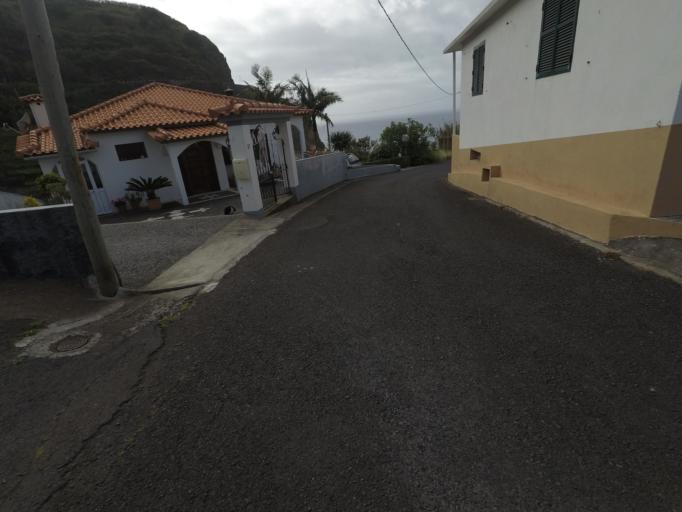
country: PT
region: Madeira
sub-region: Sao Vicente
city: Sao Vicente
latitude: 32.8263
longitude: -16.9739
